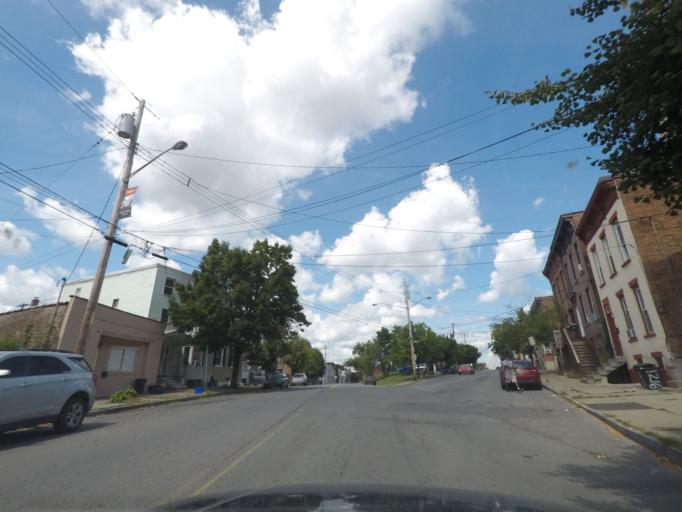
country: US
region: New York
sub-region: Rensselaer County
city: Troy
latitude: 42.7231
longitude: -73.6895
